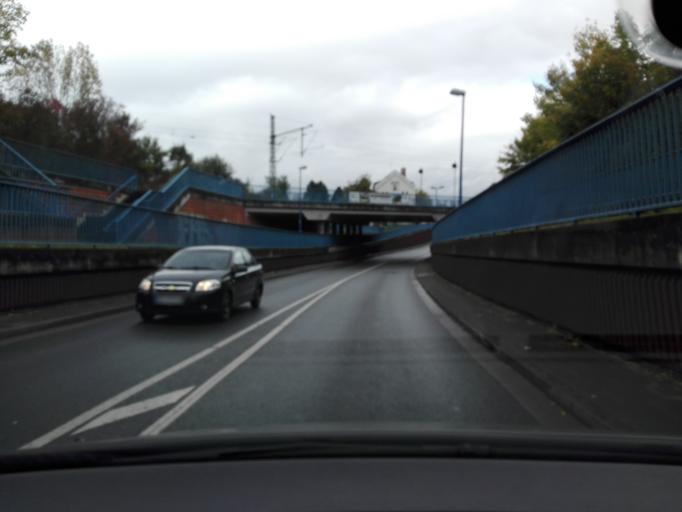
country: DE
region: North Rhine-Westphalia
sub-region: Regierungsbezirk Arnsberg
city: Unna
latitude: 51.5518
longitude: 7.6831
